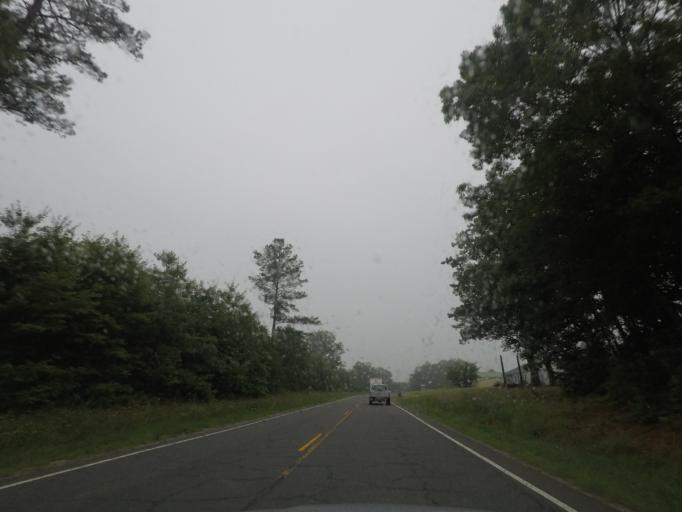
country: US
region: Virginia
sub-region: Buckingham County
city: Buckingham
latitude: 37.5078
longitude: -78.4858
